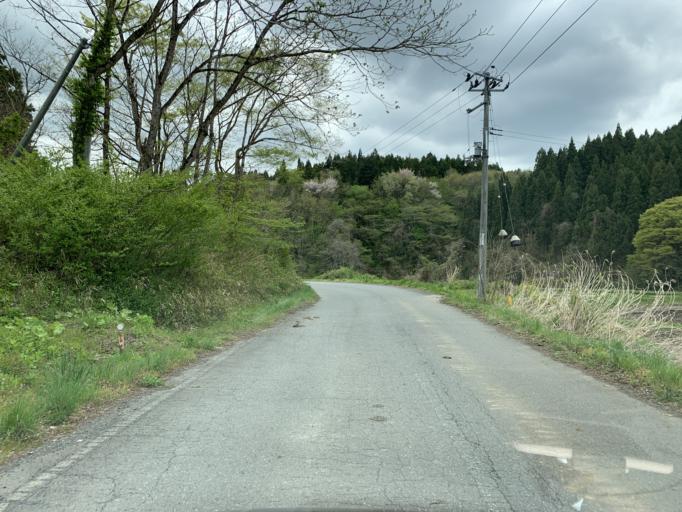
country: JP
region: Iwate
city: Ichinoseki
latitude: 38.8417
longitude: 141.3442
